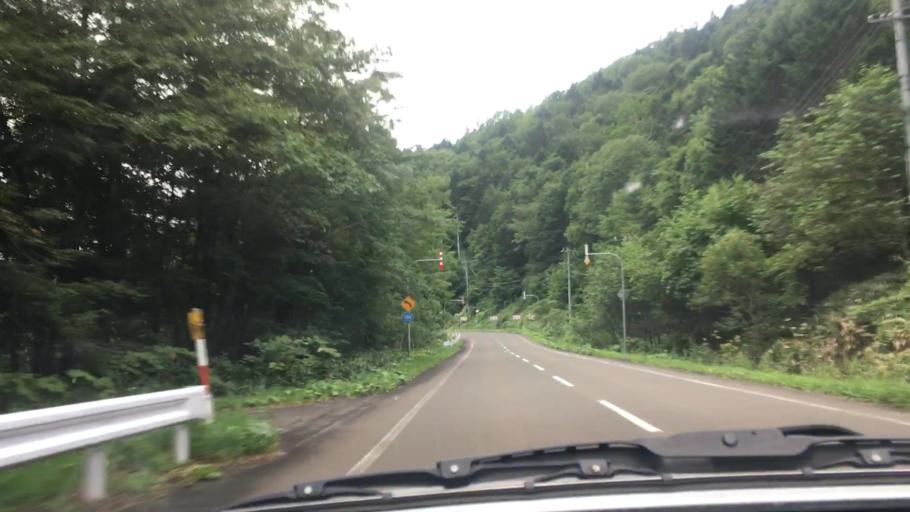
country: JP
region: Hokkaido
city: Shimo-furano
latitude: 43.0478
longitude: 142.5139
